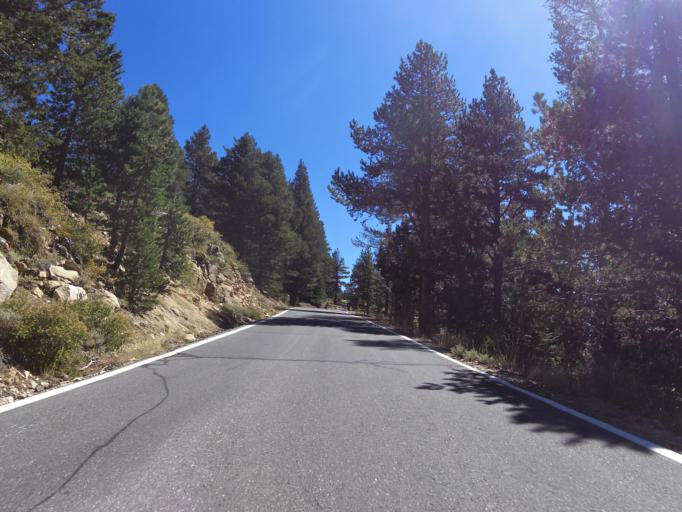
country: US
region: Nevada
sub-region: Douglas County
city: Gardnerville Ranchos
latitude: 38.5453
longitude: -119.8250
